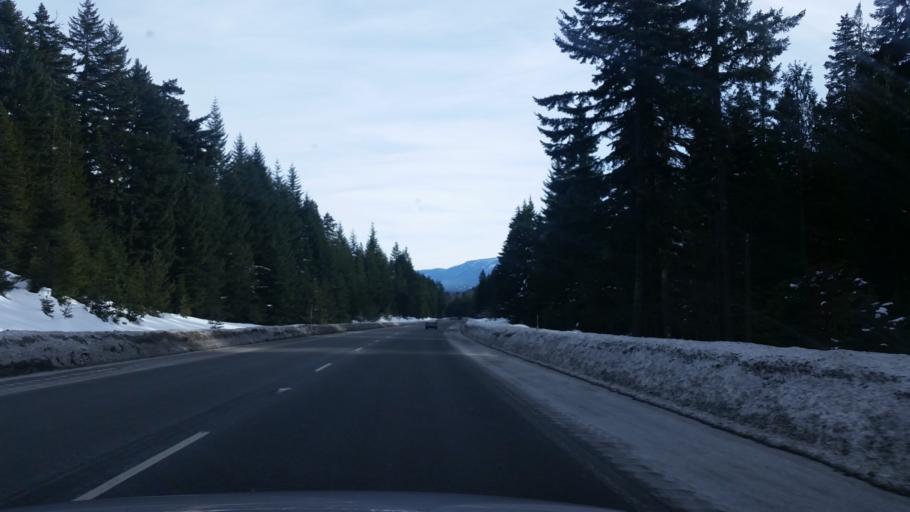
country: US
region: Washington
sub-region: Kittitas County
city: Cle Elum
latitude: 47.2634
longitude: -121.2229
